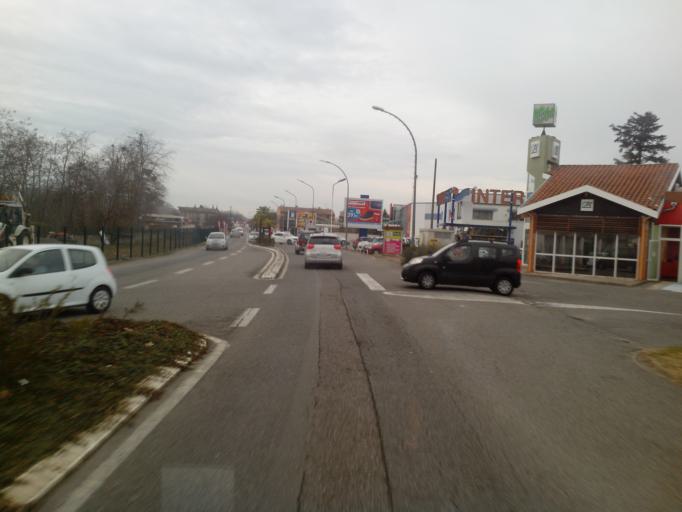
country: FR
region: Midi-Pyrenees
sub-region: Departement de l'Ariege
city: Saint-Jean-du-Falga
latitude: 43.0999
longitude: 1.6240
